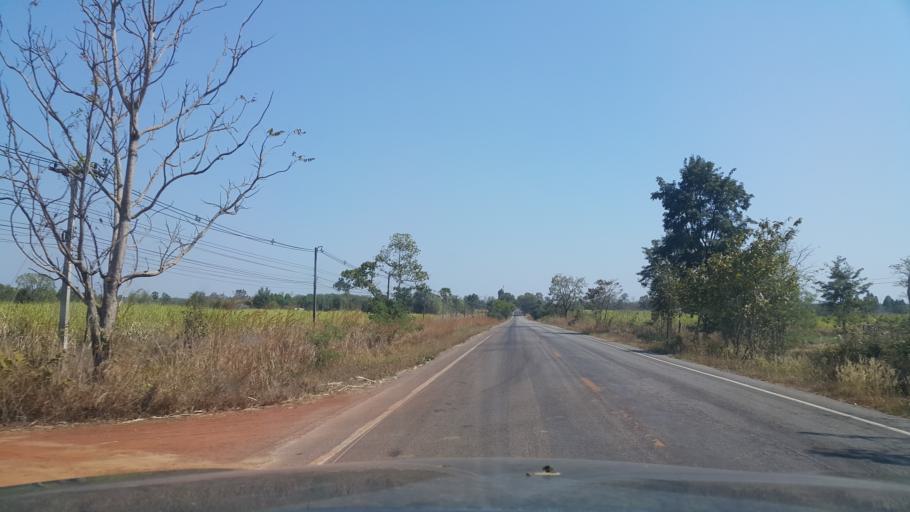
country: TH
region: Changwat Udon Thani
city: Ban Dung
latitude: 17.6089
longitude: 103.2886
